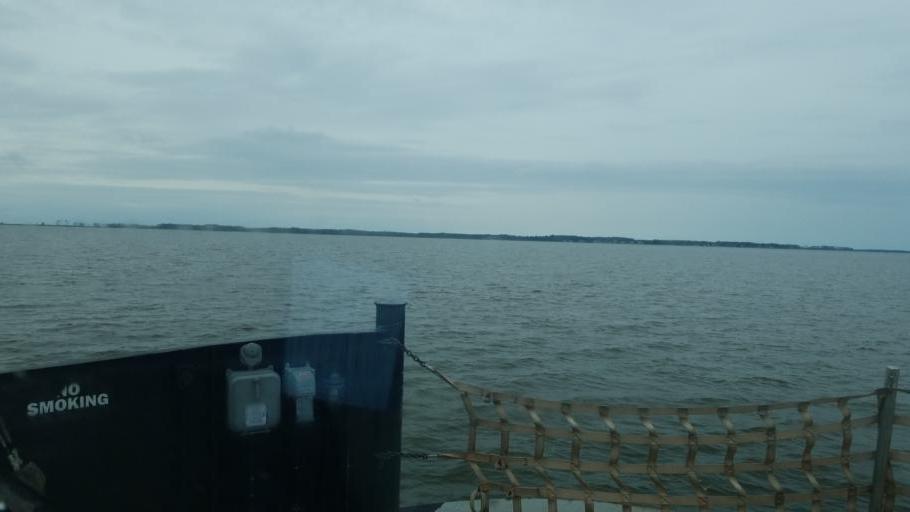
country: US
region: North Carolina
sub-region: Currituck County
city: Currituck
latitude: 36.4685
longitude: -75.9584
